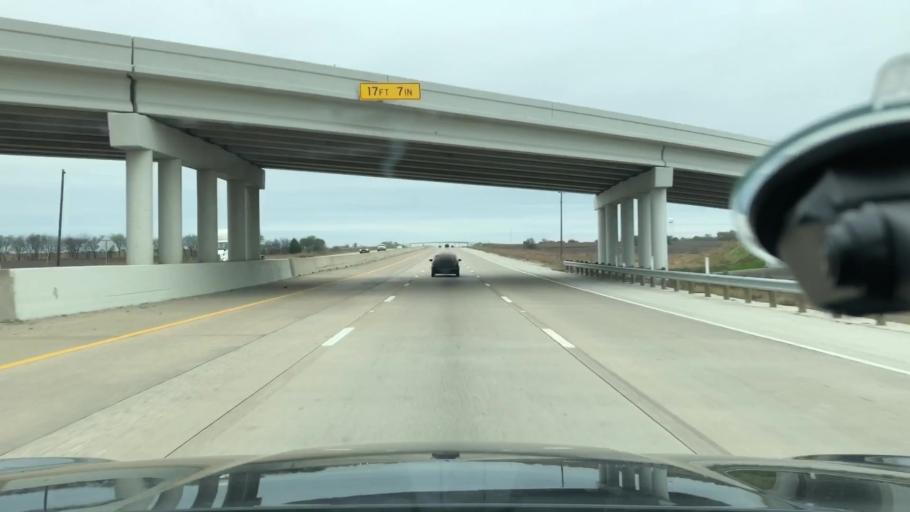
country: US
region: Texas
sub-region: Ellis County
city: Nash
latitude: 32.2899
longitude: -96.8667
